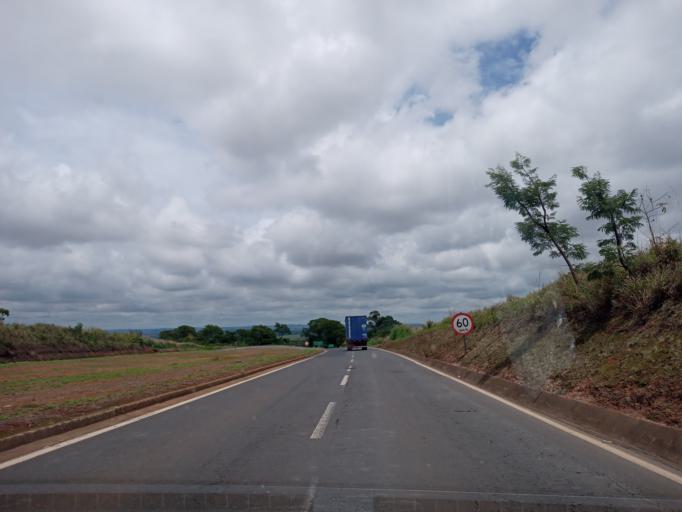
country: BR
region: Minas Gerais
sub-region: Ibia
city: Ibia
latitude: -19.5885
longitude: -46.4983
